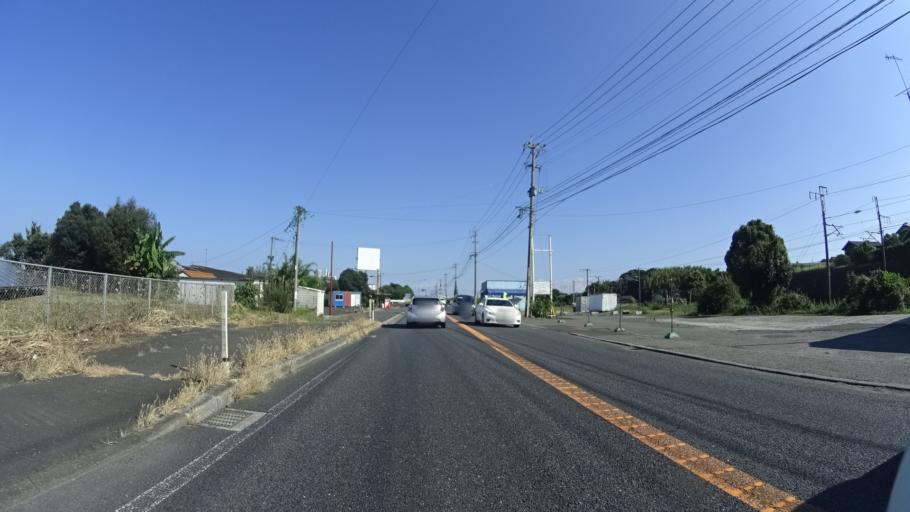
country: JP
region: Fukuoka
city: Shiida
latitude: 33.6354
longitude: 131.0753
